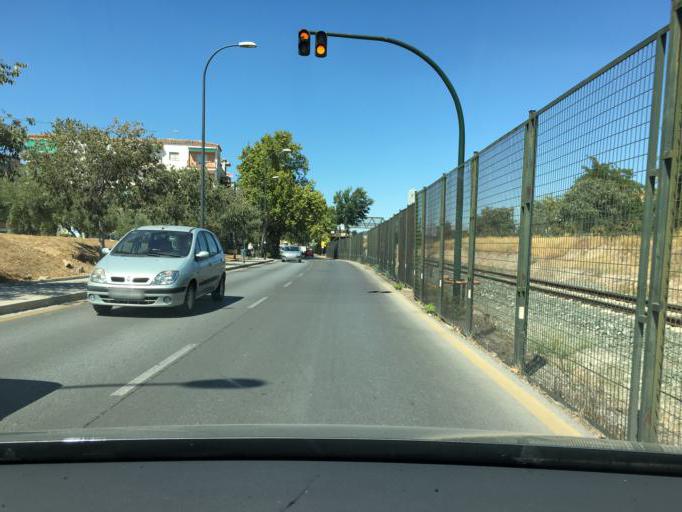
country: ES
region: Andalusia
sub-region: Provincia de Granada
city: Maracena
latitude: 37.1996
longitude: -3.6236
